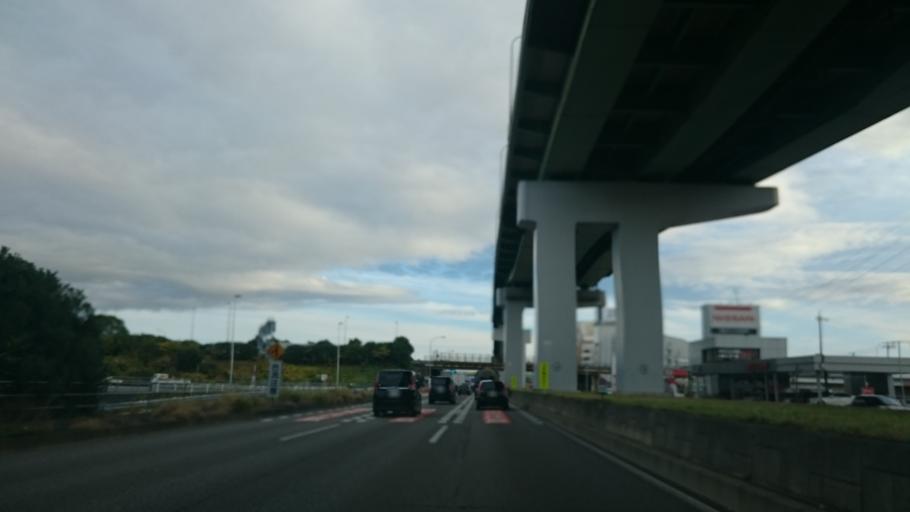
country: JP
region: Aichi
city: Komaki
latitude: 35.3016
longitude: 136.9096
